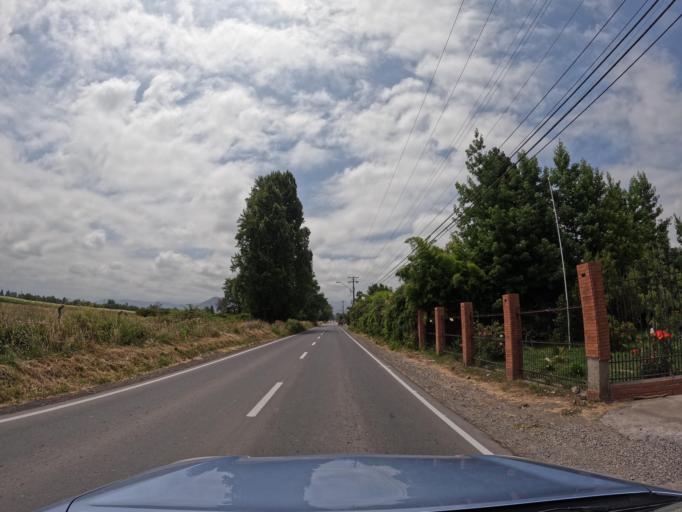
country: CL
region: O'Higgins
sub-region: Provincia de Colchagua
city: Chimbarongo
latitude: -34.7274
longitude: -71.0006
